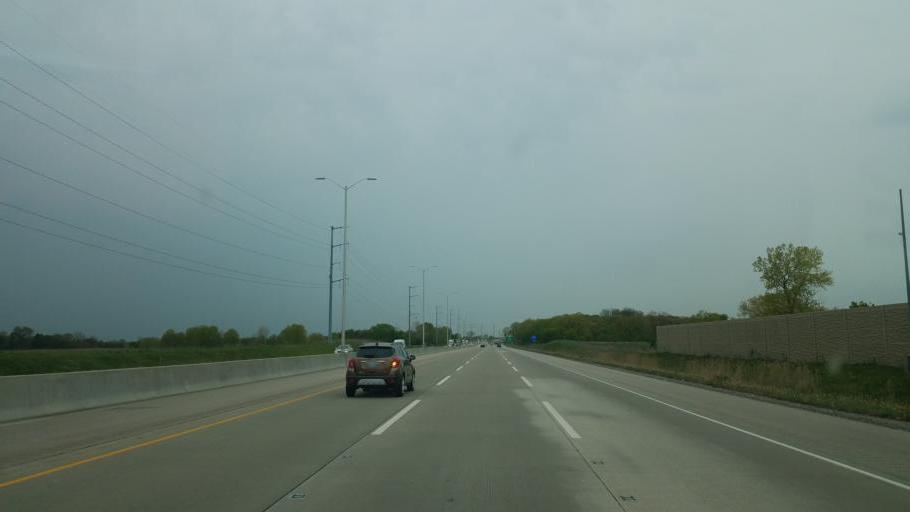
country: US
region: Illinois
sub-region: Kane County
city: Gilberts
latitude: 42.1020
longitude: -88.3850
